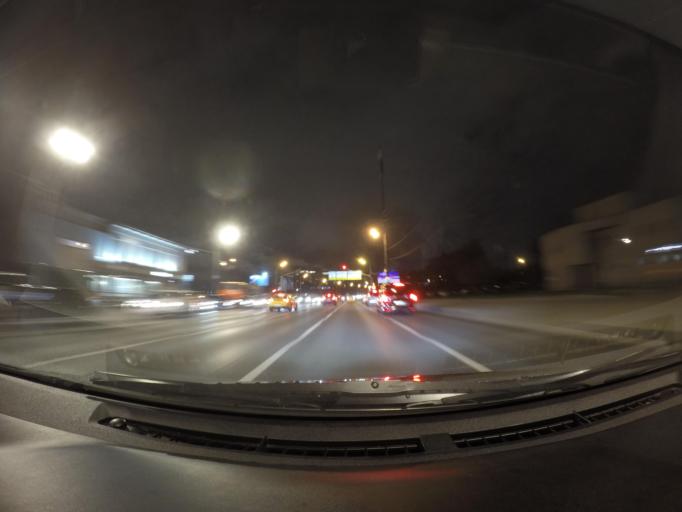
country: RU
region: Moscow
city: Tekstil'shchiki
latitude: 55.7157
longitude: 37.7114
